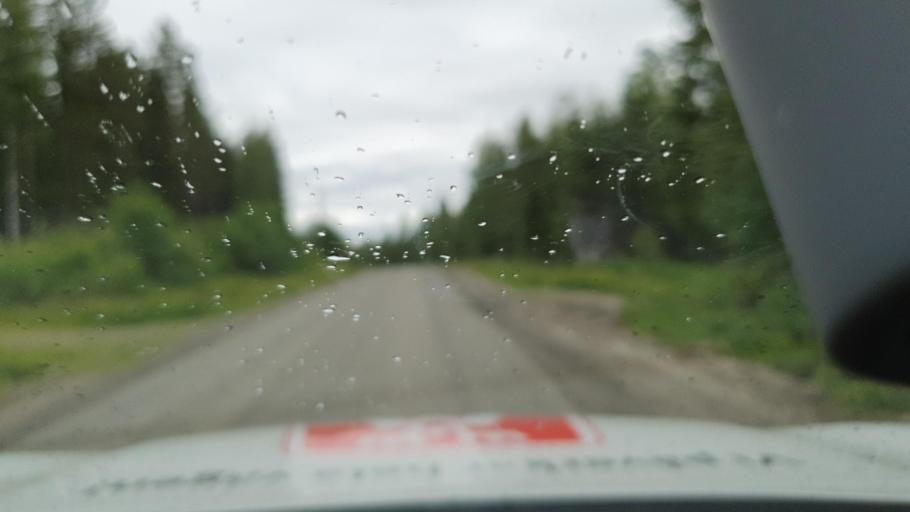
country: SE
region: Vaesterbotten
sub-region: Nordmalings Kommun
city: Nordmaling
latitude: 63.6563
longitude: 19.4414
